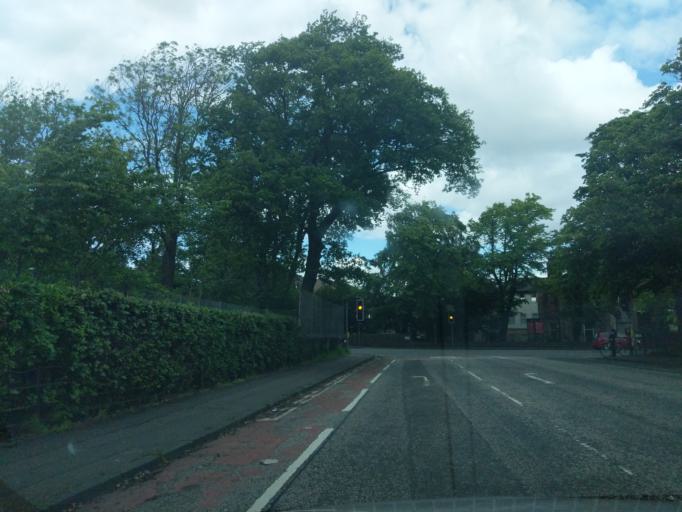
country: GB
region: Scotland
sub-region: Edinburgh
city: Edinburgh
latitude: 55.9691
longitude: -3.2256
